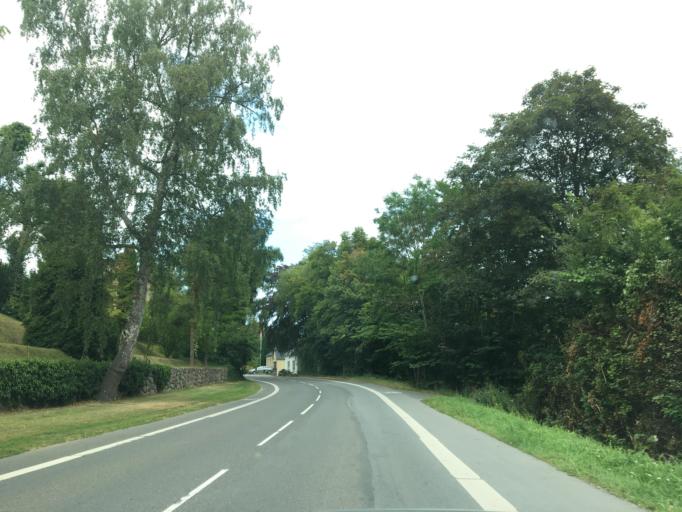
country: DK
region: South Denmark
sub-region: Nyborg Kommune
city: Nyborg
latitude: 55.3091
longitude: 10.7333
